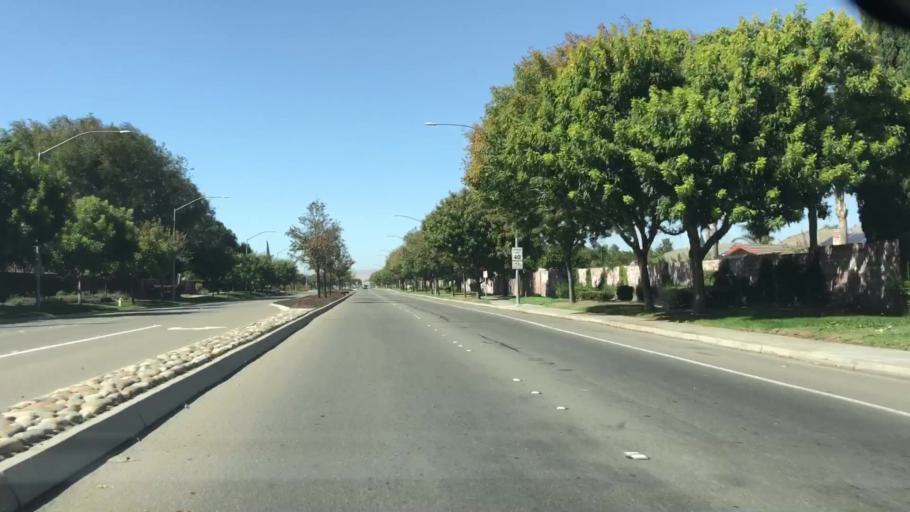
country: US
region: California
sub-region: San Joaquin County
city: Tracy
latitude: 37.7542
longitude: -121.4439
